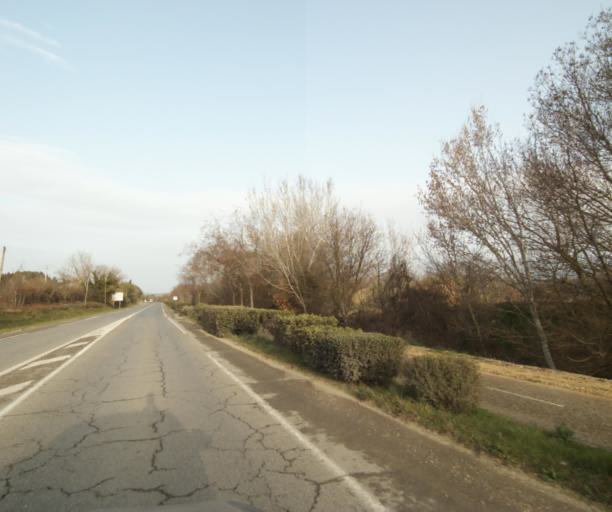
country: FR
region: Provence-Alpes-Cote d'Azur
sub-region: Departement des Bouches-du-Rhone
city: Trets
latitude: 43.4529
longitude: 5.6703
